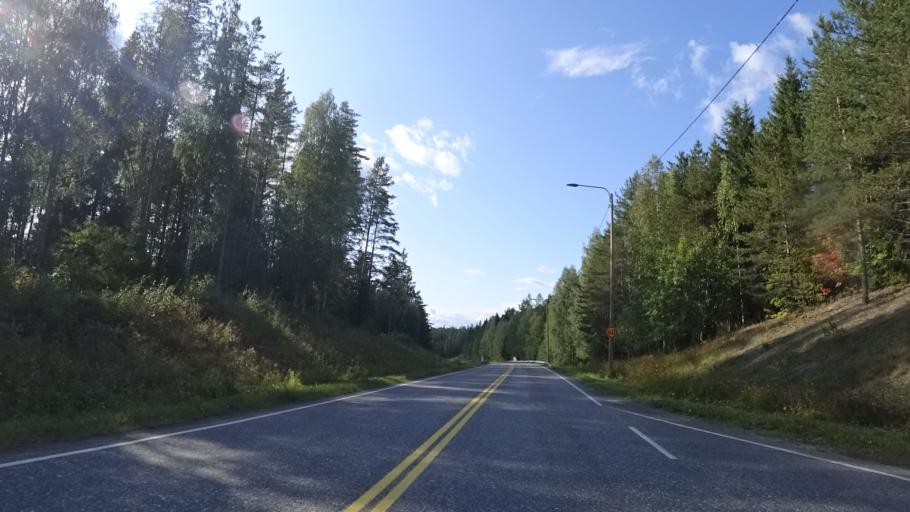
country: FI
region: North Karelia
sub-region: Keski-Karjala
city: Kitee
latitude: 62.0869
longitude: 30.1384
